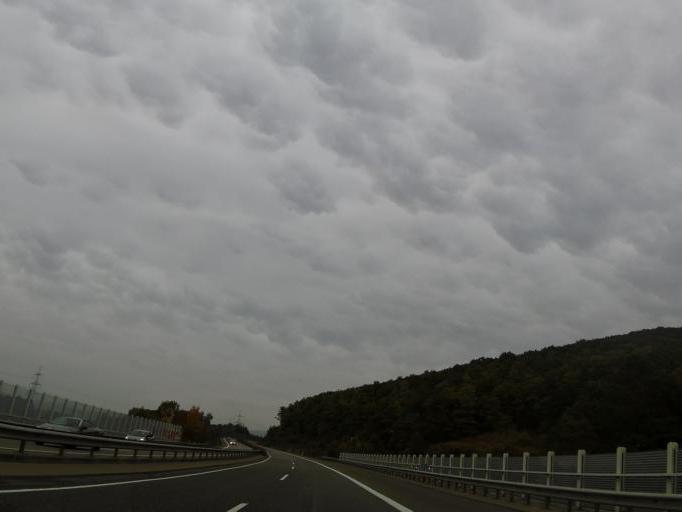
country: DE
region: Rheinland-Pfalz
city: Wartenberg-Rohrbach
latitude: 49.5406
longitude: 7.8551
